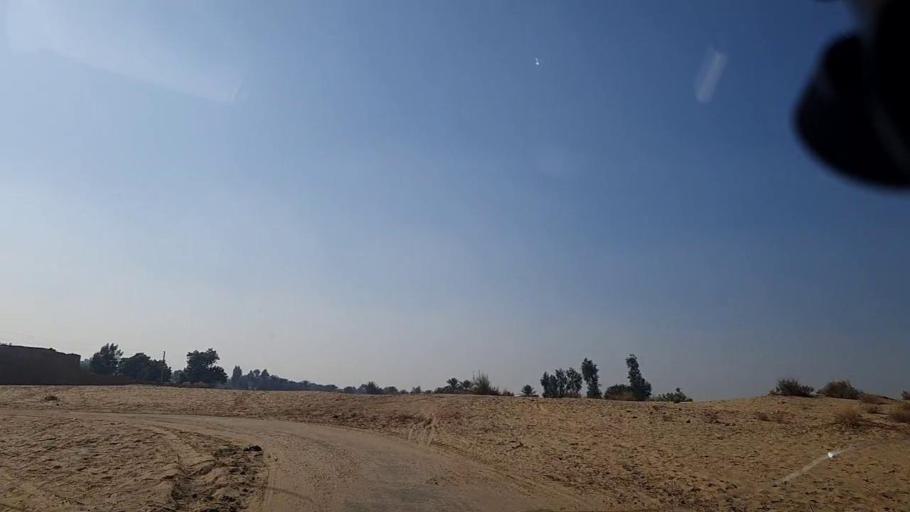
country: PK
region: Sindh
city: Khanpur
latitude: 27.7283
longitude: 69.4399
